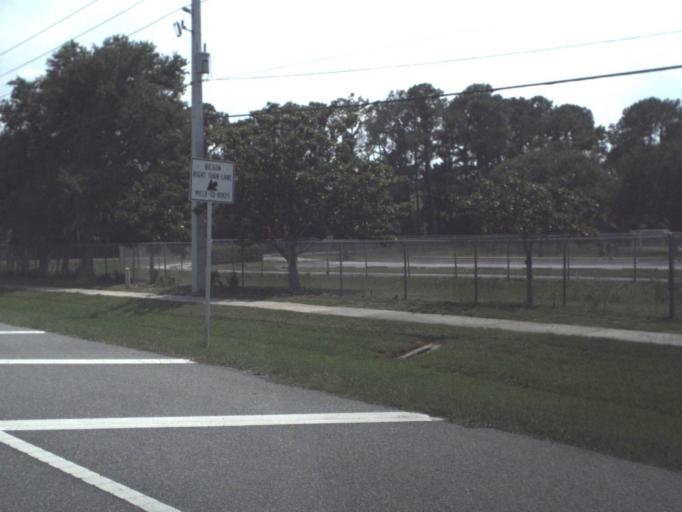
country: US
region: Florida
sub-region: Saint Johns County
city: Sawgrass
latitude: 30.2139
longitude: -81.3809
